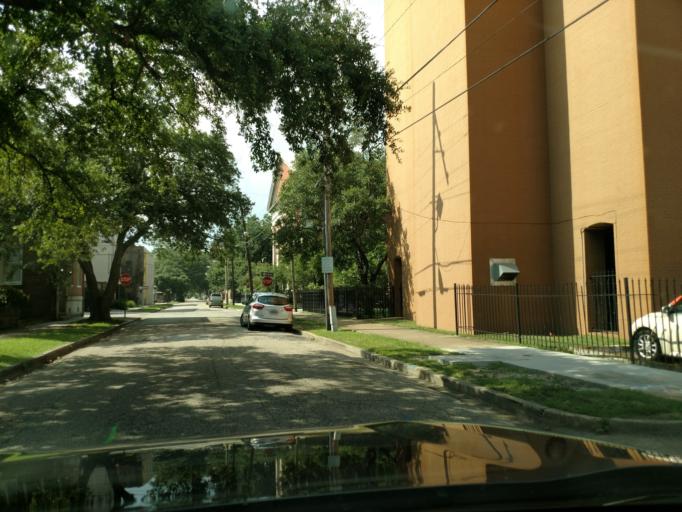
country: US
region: Alabama
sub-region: Mobile County
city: Mobile
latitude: 30.6893
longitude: -88.0459
